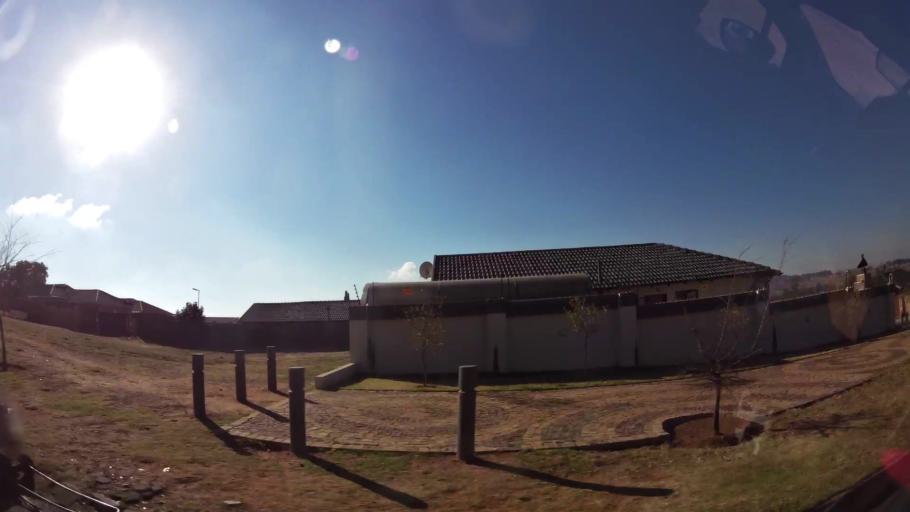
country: ZA
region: Gauteng
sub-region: City of Johannesburg Metropolitan Municipality
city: Roodepoort
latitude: -26.1576
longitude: 27.8328
